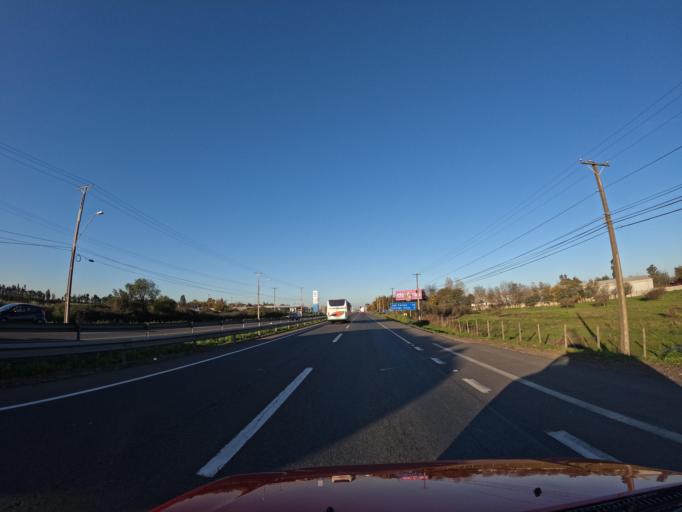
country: CL
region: Biobio
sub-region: Provincia de Nuble
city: Chillan
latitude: -36.6356
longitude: -72.1958
